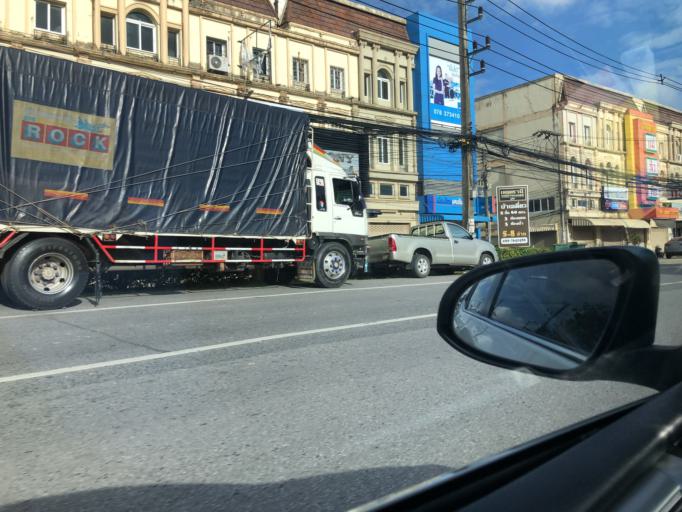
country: TH
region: Phuket
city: Ban Ko Kaeo
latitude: 7.9232
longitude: 98.3962
